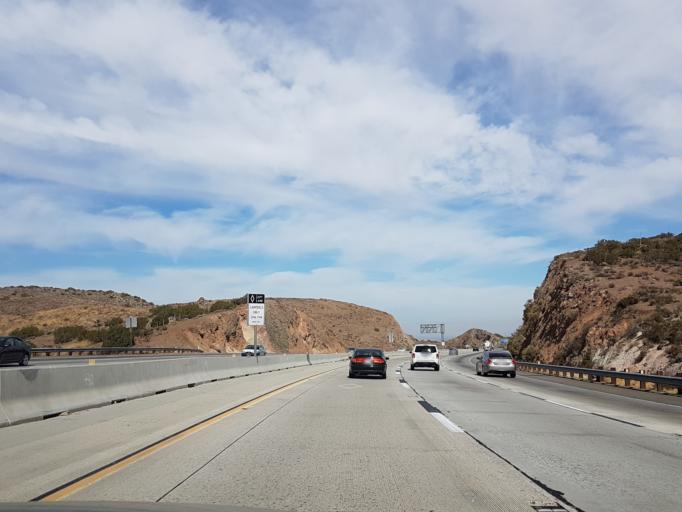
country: US
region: California
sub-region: Los Angeles County
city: Vincent
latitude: 34.5269
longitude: -118.1132
